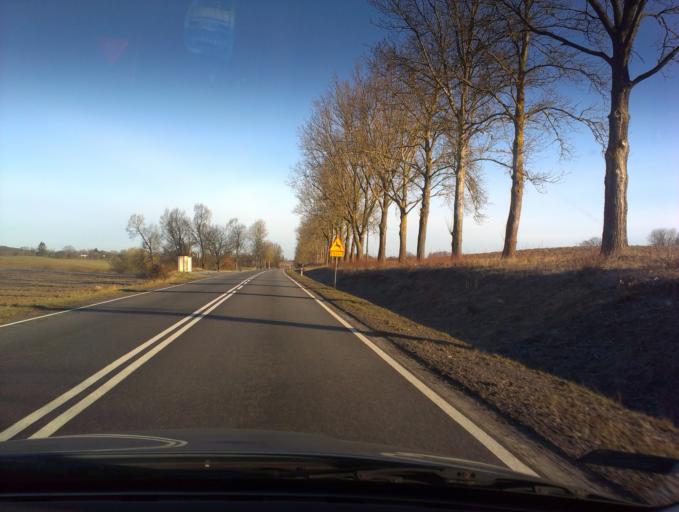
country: PL
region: West Pomeranian Voivodeship
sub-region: Powiat koszalinski
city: Bobolice
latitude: 53.9341
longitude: 16.5962
